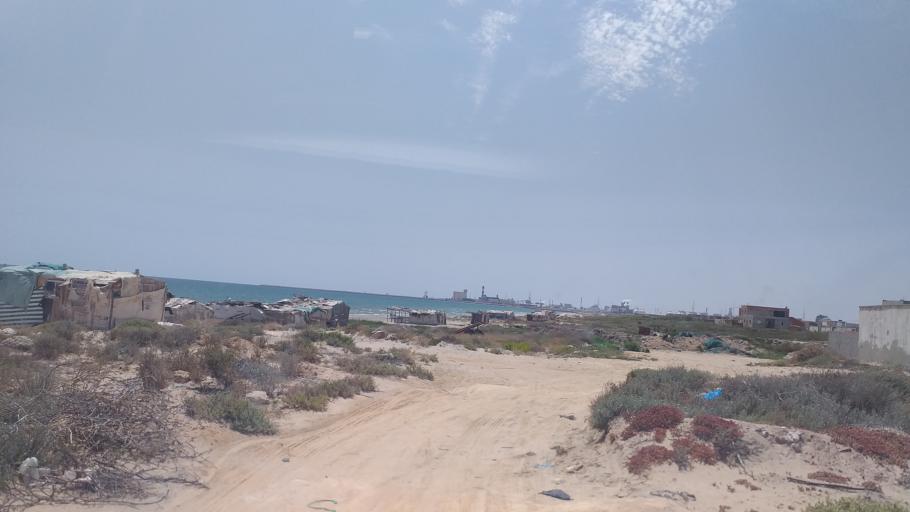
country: TN
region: Qabis
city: Gabes
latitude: 33.9480
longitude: 10.0746
